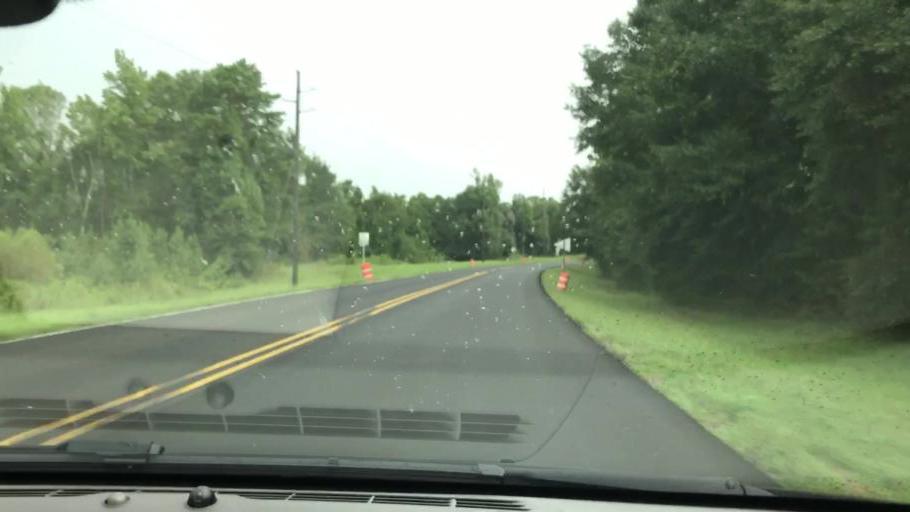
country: US
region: Georgia
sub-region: Clay County
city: Fort Gaines
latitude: 31.5222
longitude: -85.0245
